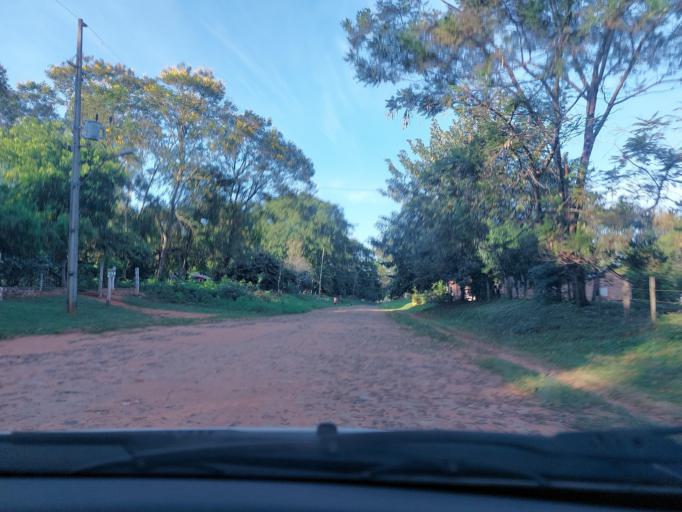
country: PY
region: San Pedro
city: Itacurubi del Rosario
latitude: -24.5604
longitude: -56.5911
